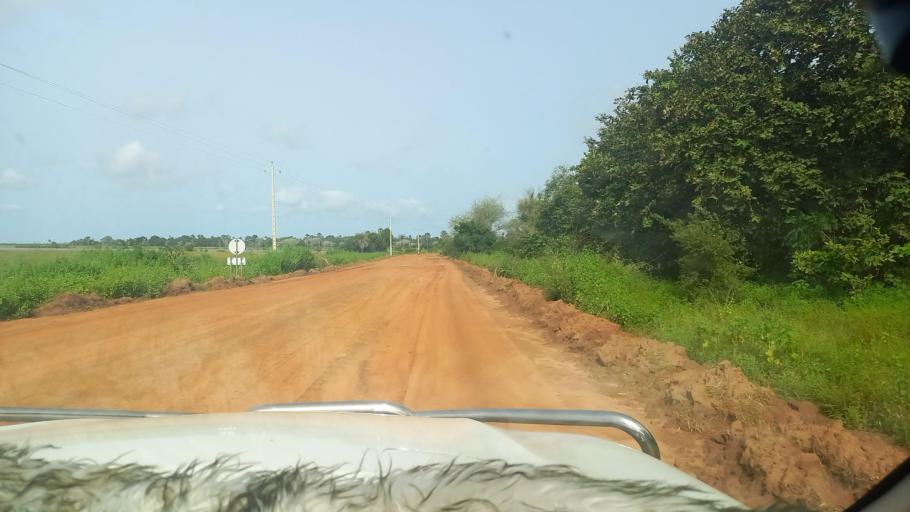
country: SN
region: Ziguinchor
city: Ziguinchor
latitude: 12.6709
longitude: -16.2770
